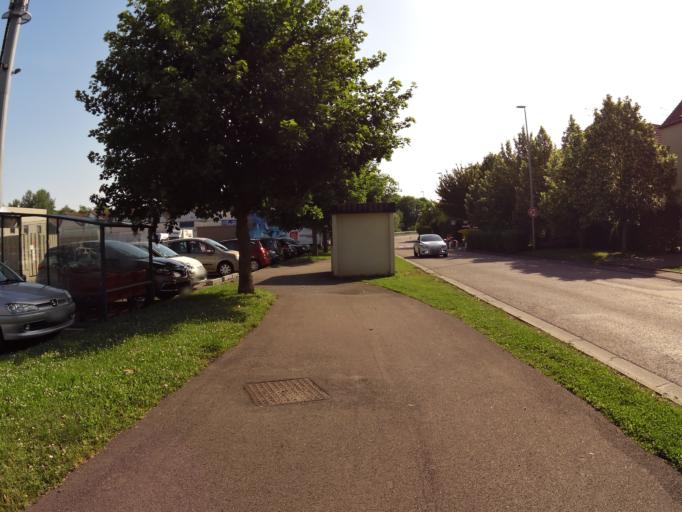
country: FR
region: Champagne-Ardenne
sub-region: Departement de l'Aube
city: Saint-Julien-les-Villas
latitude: 48.2808
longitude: 4.0968
